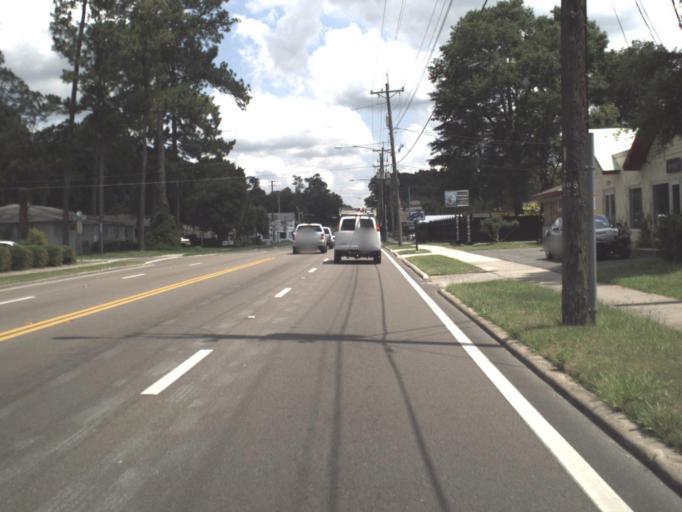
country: US
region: Florida
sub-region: Alachua County
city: Gainesville
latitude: 29.6713
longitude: -82.3308
